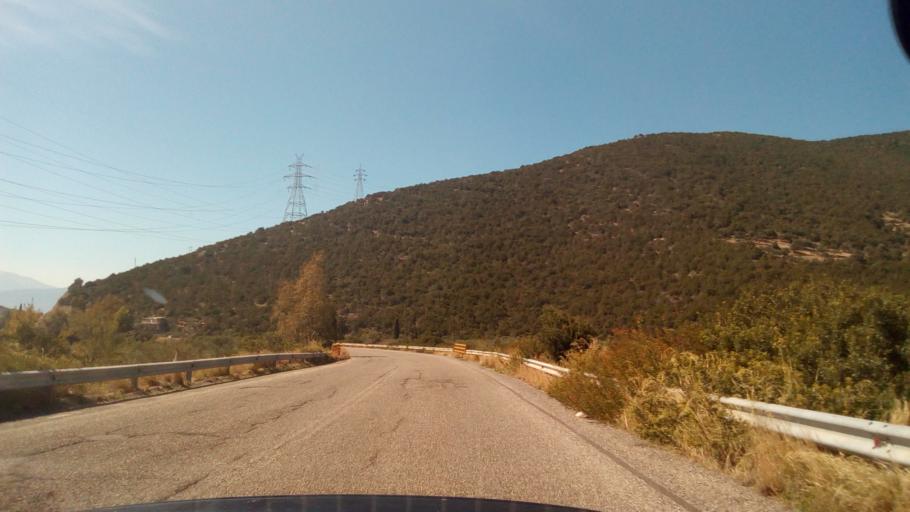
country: GR
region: West Greece
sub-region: Nomos Achaias
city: Selianitika
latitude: 38.3701
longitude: 22.1228
